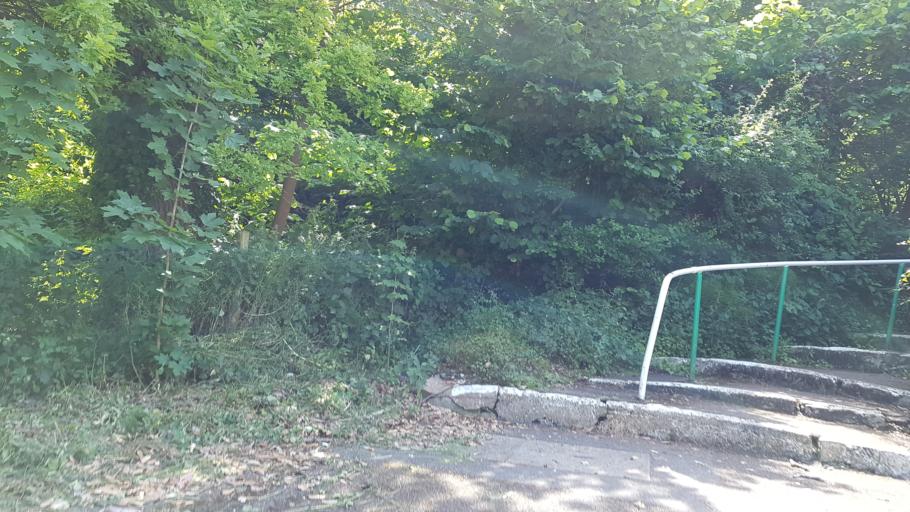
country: GB
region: England
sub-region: Isle of Wight
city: Cowes
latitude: 50.7661
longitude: -1.3082
